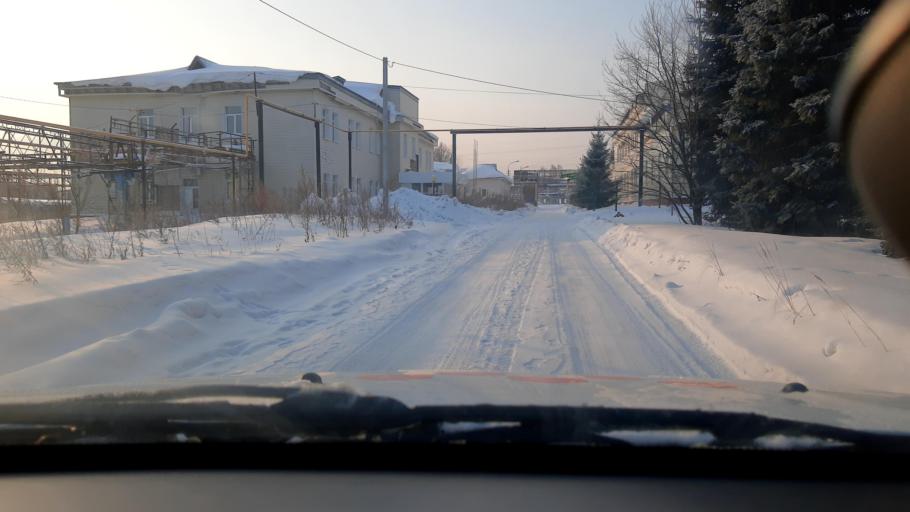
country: RU
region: Bashkortostan
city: Ufa
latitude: 54.8394
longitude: 56.0978
